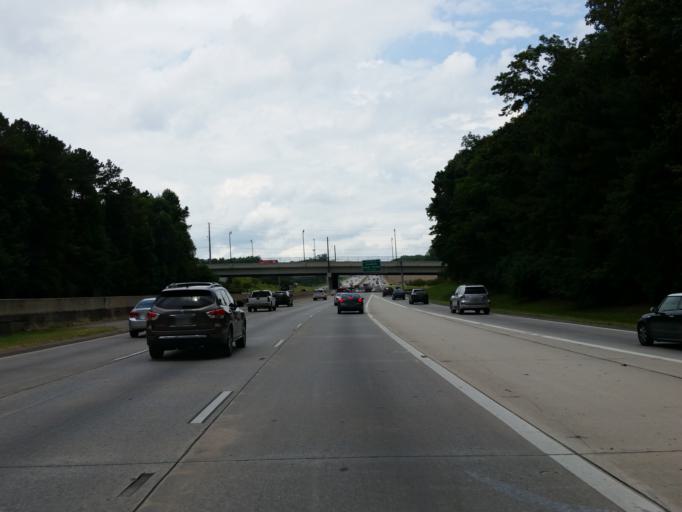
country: US
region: Georgia
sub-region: Fulton County
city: Sandy Springs
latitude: 33.9170
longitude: -84.3577
